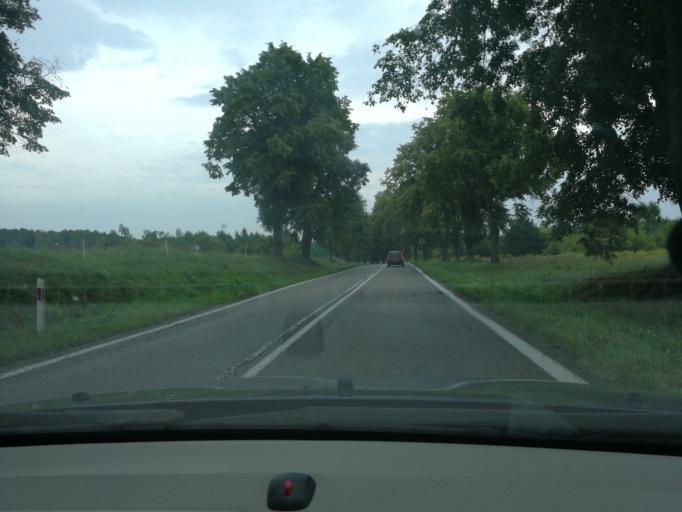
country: PL
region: Masovian Voivodeship
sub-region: Powiat zyrardowski
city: Radziejowice
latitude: 52.0353
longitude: 20.5802
